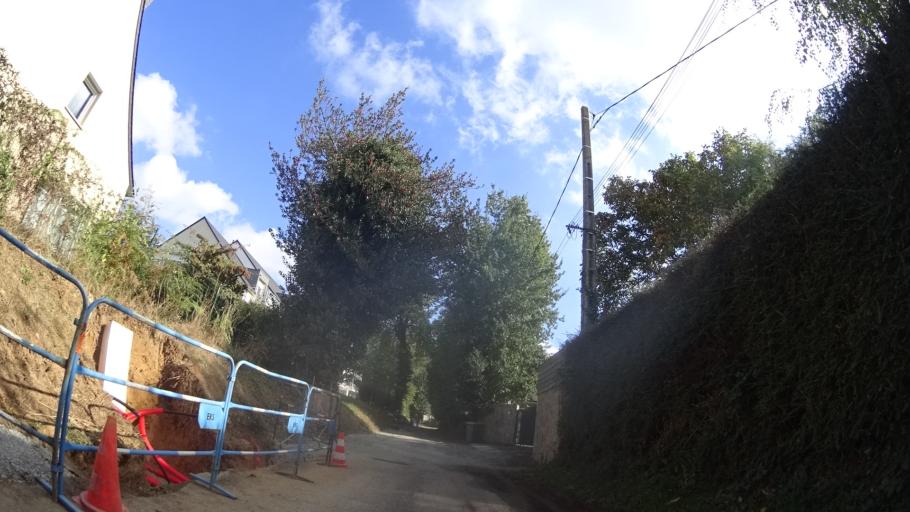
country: FR
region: Brittany
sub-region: Departement d'Ille-et-Vilaine
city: Geveze
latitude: 48.2210
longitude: -1.7766
